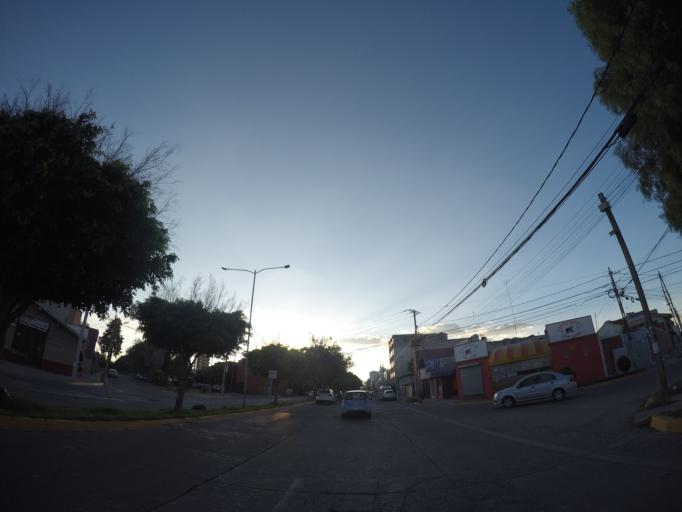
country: MX
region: San Luis Potosi
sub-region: San Luis Potosi
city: San Luis Potosi
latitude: 22.1411
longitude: -100.9950
